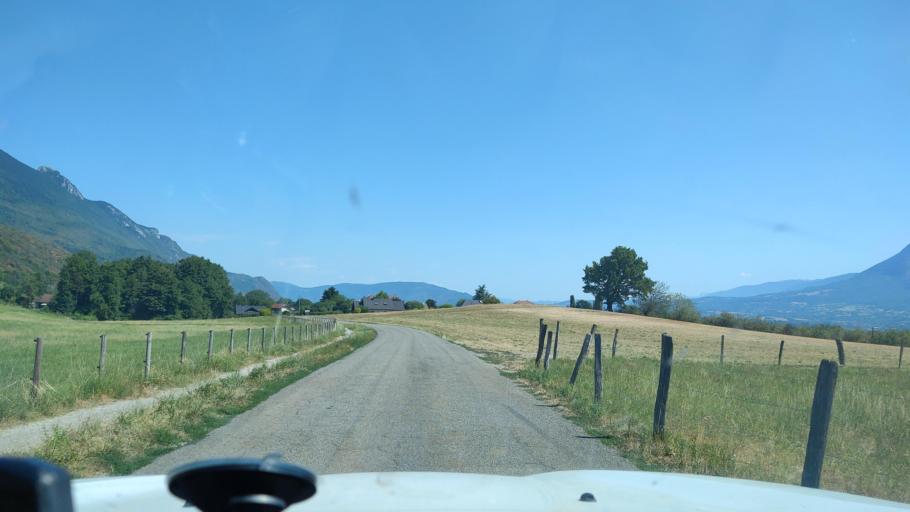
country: FR
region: Rhone-Alpes
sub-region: Departement de la Savoie
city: Le Bourget-du-Lac
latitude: 45.6196
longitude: 5.8498
